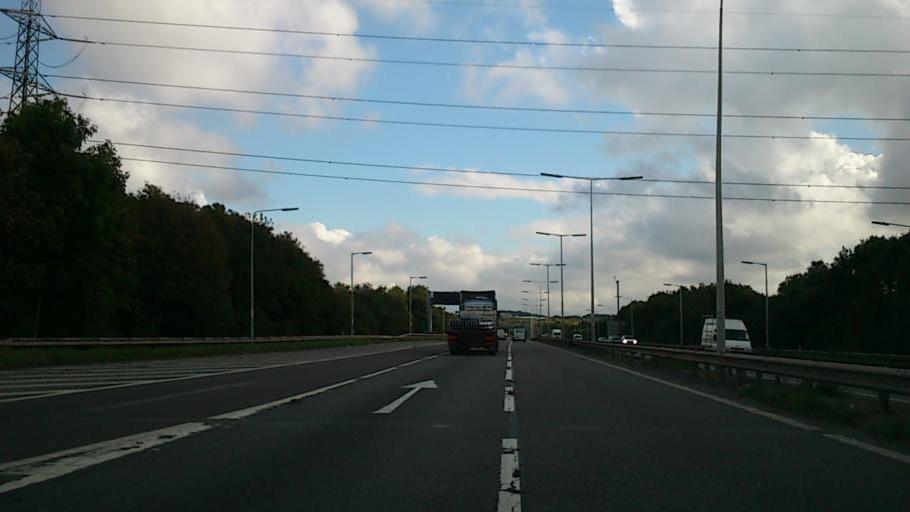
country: GB
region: England
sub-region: Staffordshire
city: Featherstone
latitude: 52.6383
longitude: -2.1182
